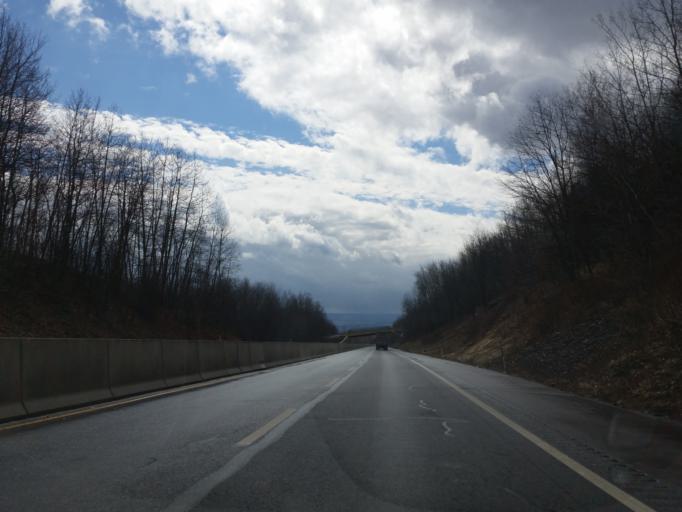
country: US
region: Pennsylvania
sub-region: Lackawanna County
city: Taylor
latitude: 41.4145
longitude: -75.7189
